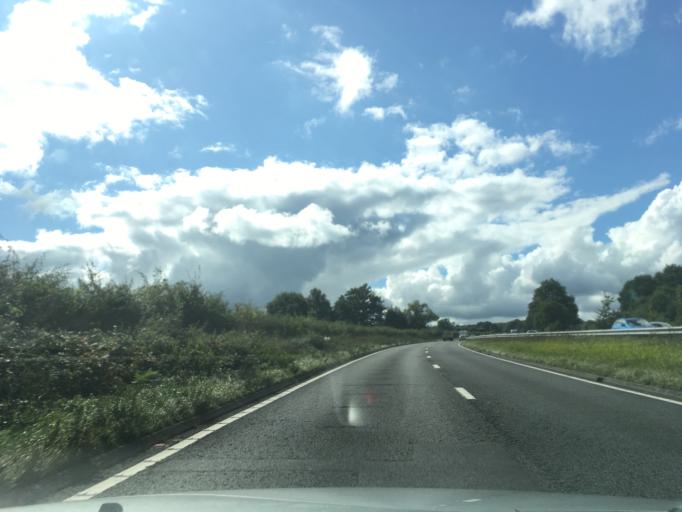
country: GB
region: England
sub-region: Surrey
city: Hindhead
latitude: 51.1402
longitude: -0.7070
